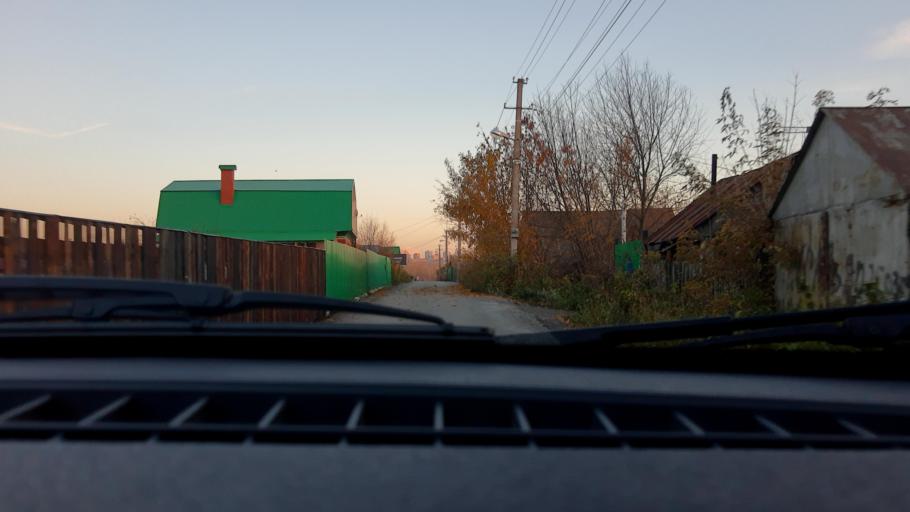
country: RU
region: Bashkortostan
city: Mikhaylovka
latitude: 54.7587
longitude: 55.9076
